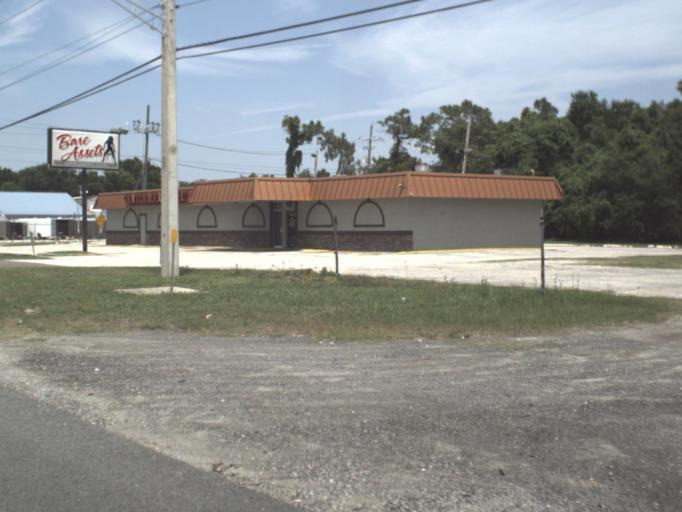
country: US
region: Florida
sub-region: Duval County
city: Jacksonville
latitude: 30.4312
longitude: -81.6444
